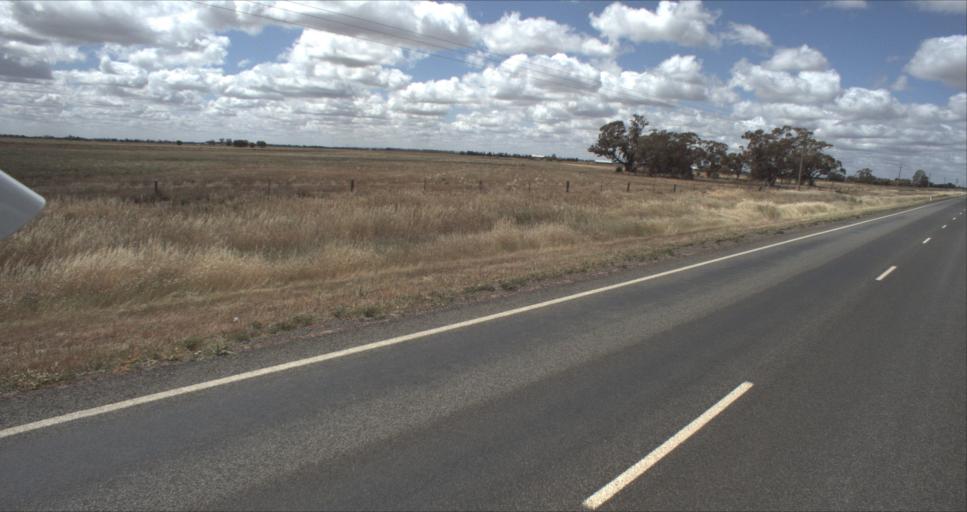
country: AU
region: New South Wales
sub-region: Murrumbidgee Shire
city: Darlington Point
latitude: -34.4830
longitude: 146.1565
